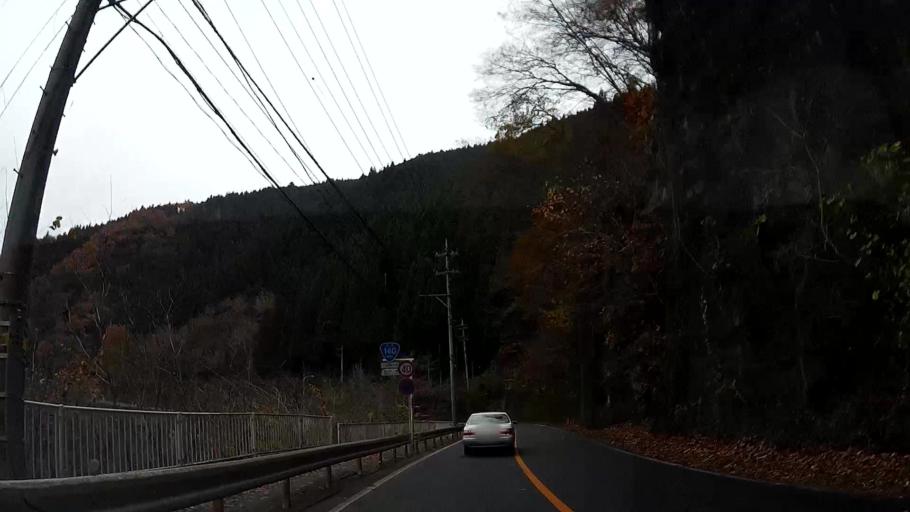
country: JP
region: Saitama
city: Chichibu
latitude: 35.9444
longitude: 138.9422
